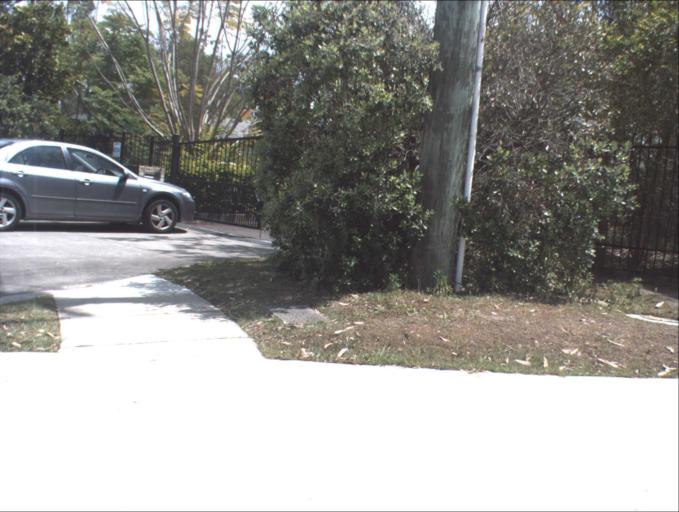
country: AU
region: Queensland
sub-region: Logan
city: Slacks Creek
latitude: -27.6522
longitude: 153.1677
